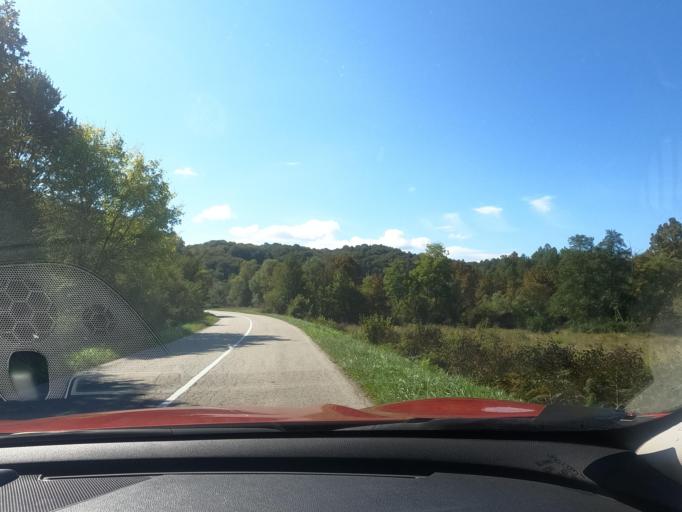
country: BA
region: Federation of Bosnia and Herzegovina
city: Vrnograc
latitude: 45.2684
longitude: 15.9713
